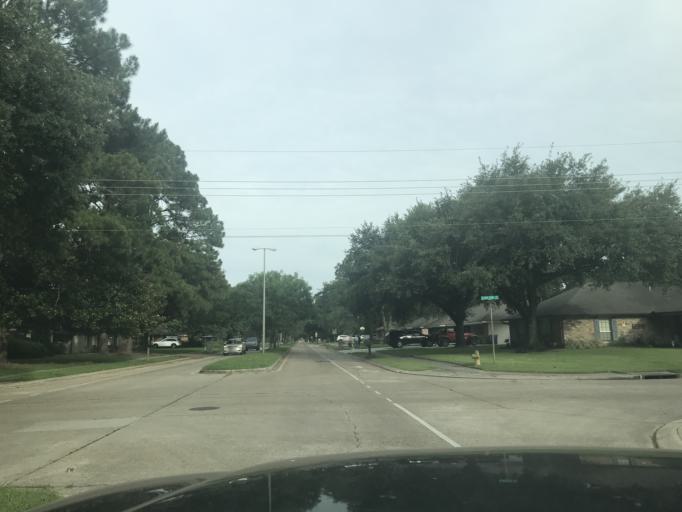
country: US
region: Louisiana
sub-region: Lafayette Parish
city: Lafayette
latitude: 30.1970
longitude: -92.0481
